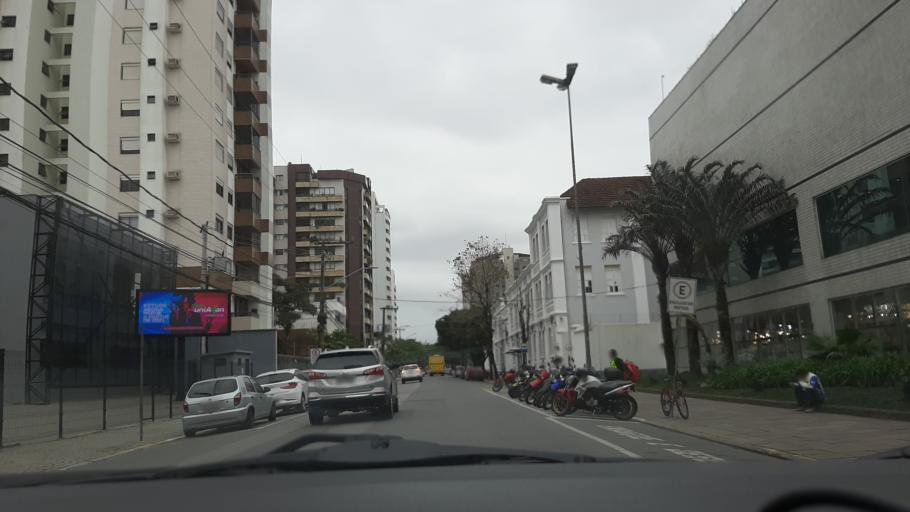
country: BR
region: Santa Catarina
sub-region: Joinville
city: Joinville
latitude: -26.3045
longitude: -48.8490
